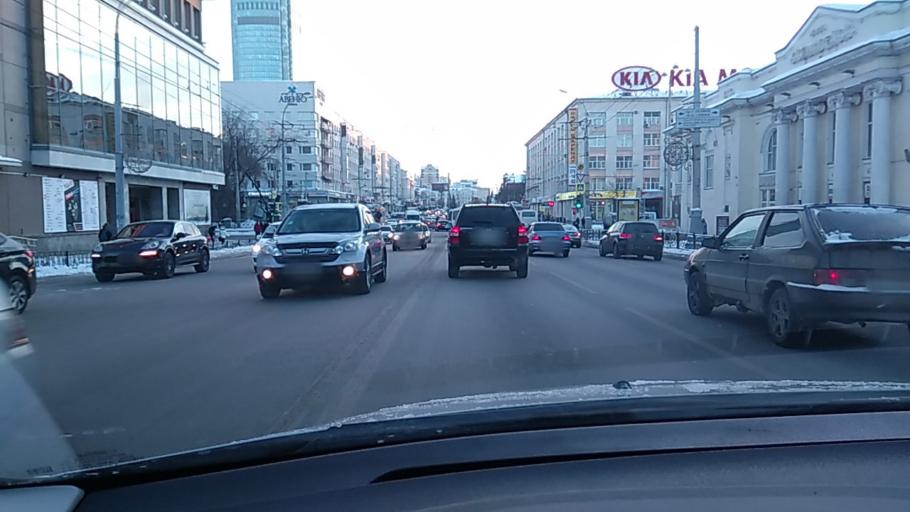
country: RU
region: Sverdlovsk
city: Yekaterinburg
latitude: 56.8413
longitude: 60.6128
